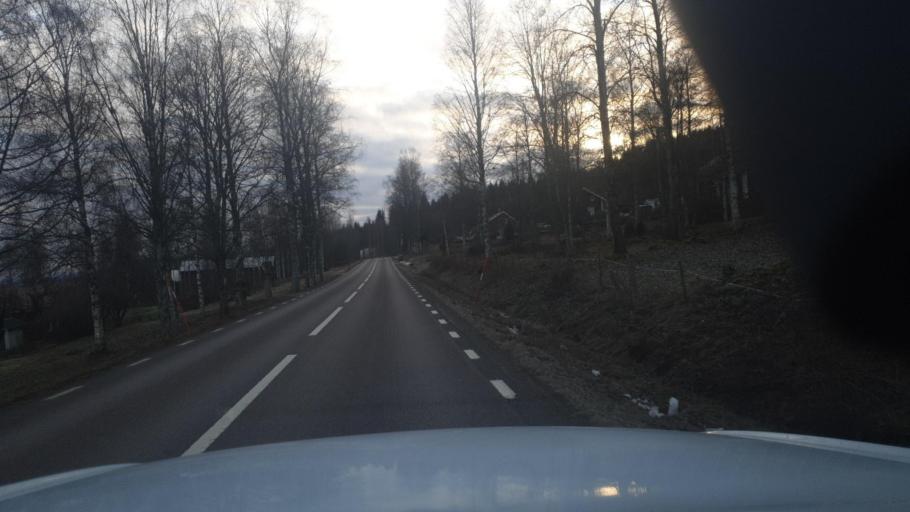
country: SE
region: Vaermland
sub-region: Torsby Kommun
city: Torsby
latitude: 59.9202
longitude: 12.8977
